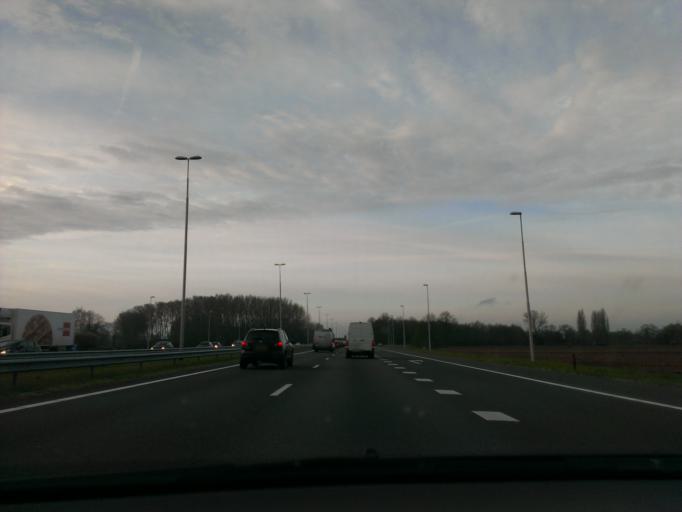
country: NL
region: Gelderland
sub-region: Gemeente Epe
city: Emst
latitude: 52.2970
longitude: 6.0089
